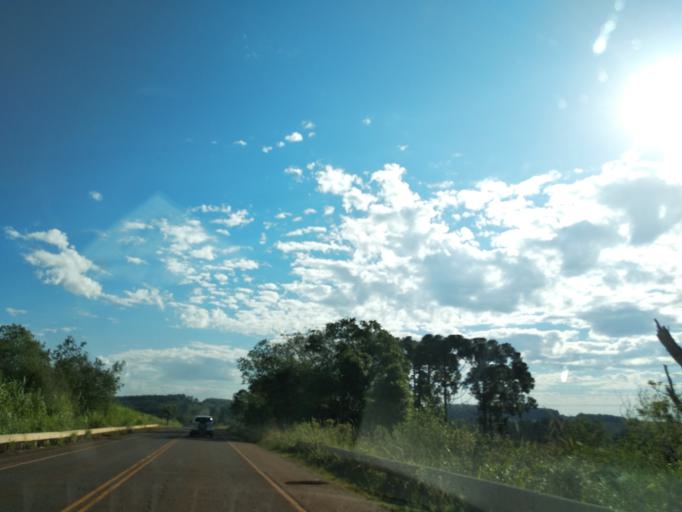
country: AR
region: Misiones
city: Ruiz de Montoya
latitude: -27.0590
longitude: -55.0259
